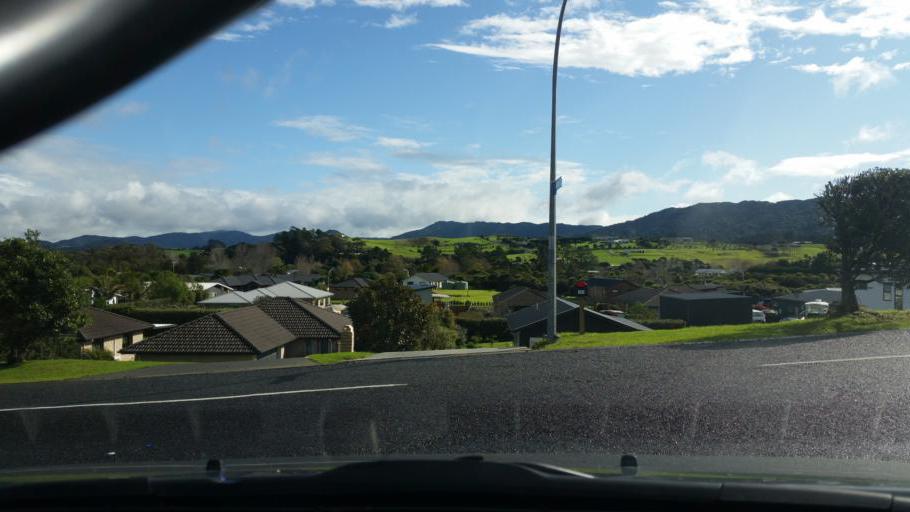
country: NZ
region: Auckland
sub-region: Auckland
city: Wellsford
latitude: -36.0884
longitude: 174.5768
